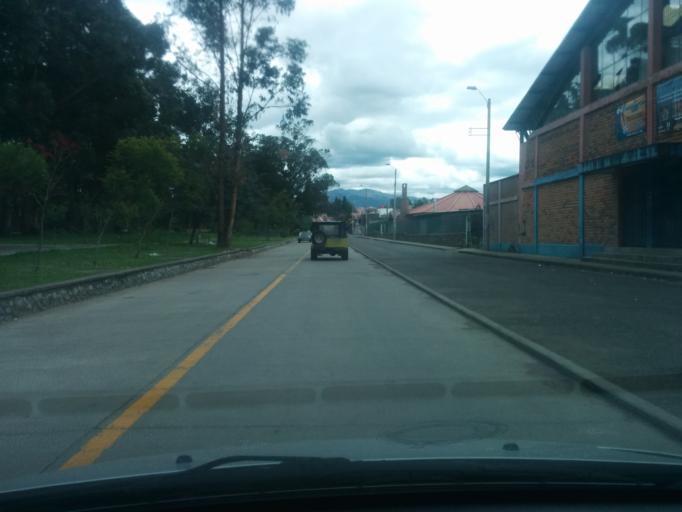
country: EC
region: Azuay
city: Cuenca
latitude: -2.8914
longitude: -78.9598
